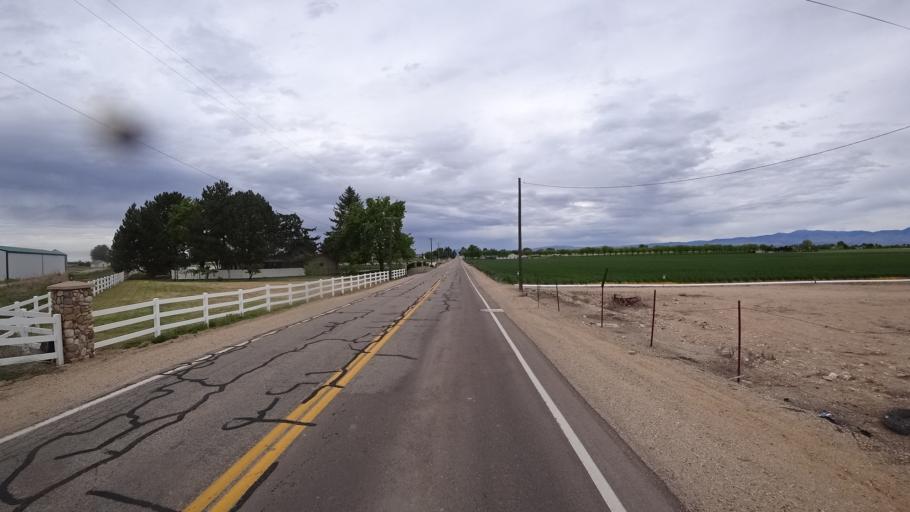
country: US
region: Idaho
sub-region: Ada County
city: Meridian
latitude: 43.5668
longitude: -116.4138
